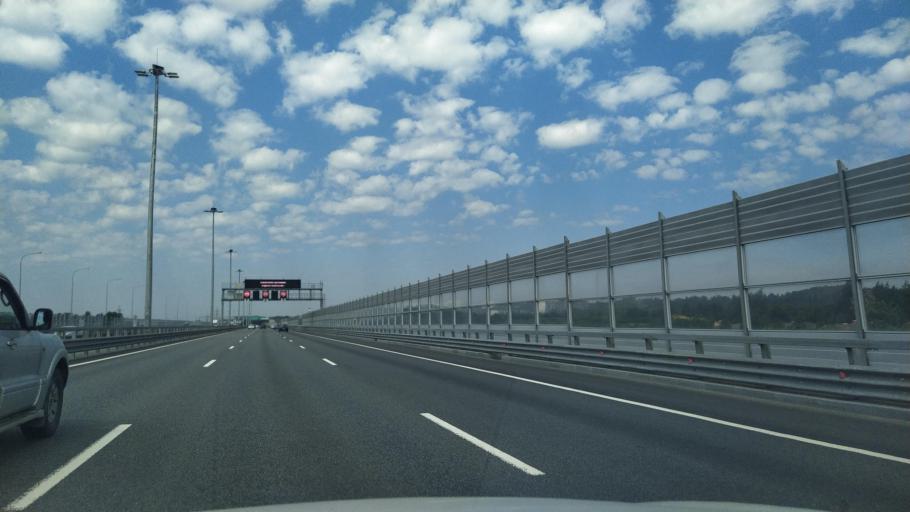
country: RU
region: St.-Petersburg
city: Pargolovo
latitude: 60.0969
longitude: 30.3067
